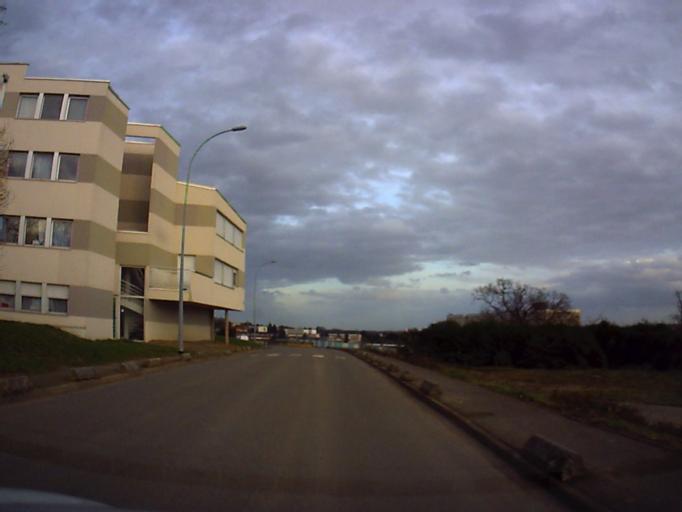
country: FR
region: Brittany
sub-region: Departement d'Ille-et-Vilaine
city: Rennes
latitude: 48.1226
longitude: -1.6442
